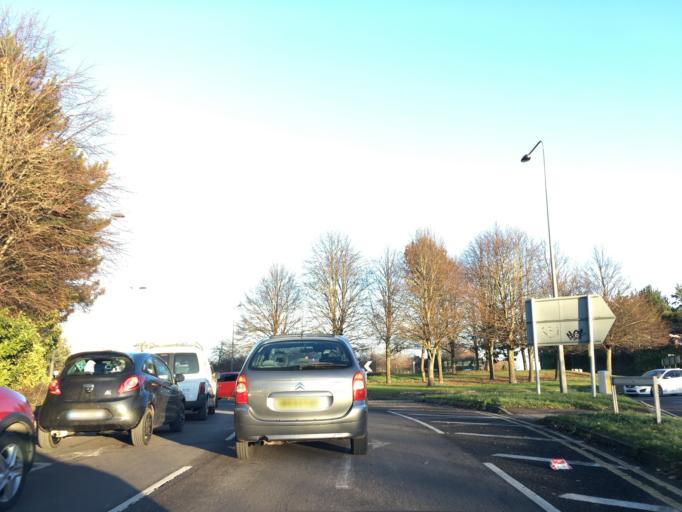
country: GB
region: England
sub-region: South Gloucestershire
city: Stoke Gifford
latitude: 51.5096
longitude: -2.5513
